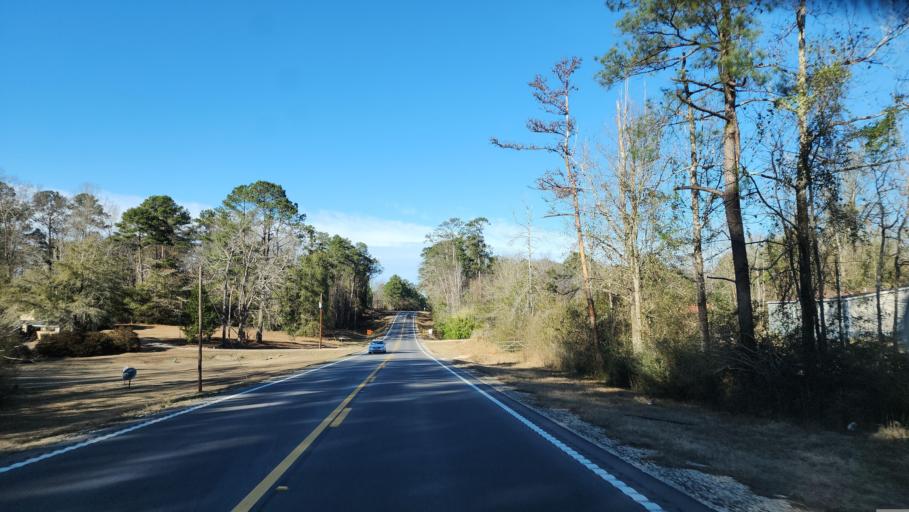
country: US
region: Mississippi
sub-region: Wayne County
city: Waynesboro
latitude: 31.7135
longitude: -88.6447
